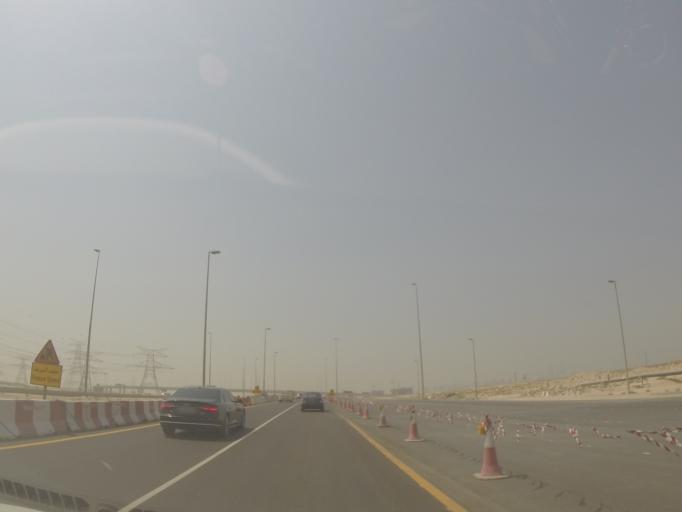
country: AE
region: Dubai
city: Dubai
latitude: 25.0127
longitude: 55.1652
